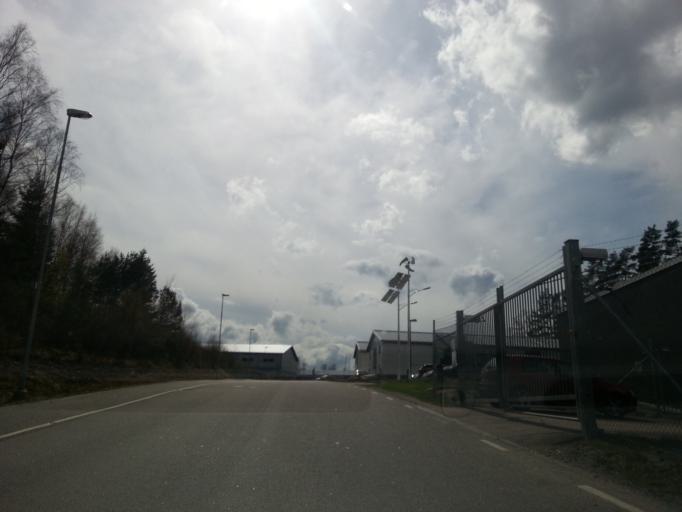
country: SE
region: Vaestra Goetaland
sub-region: Kungalvs Kommun
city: Kungalv
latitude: 57.8832
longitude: 11.9368
